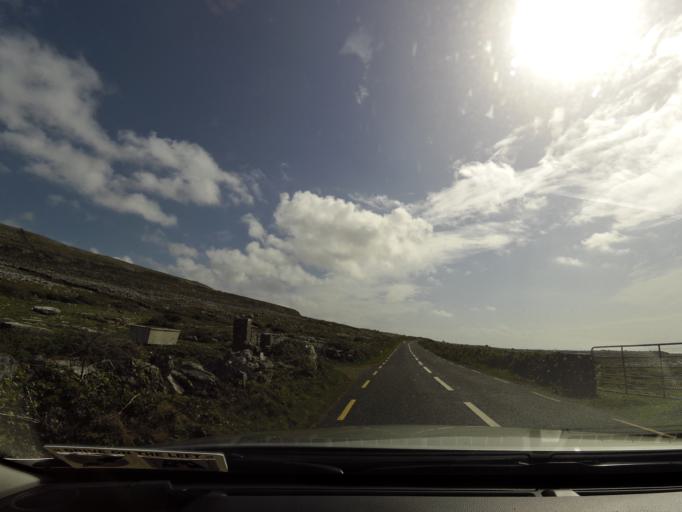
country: IE
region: Connaught
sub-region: County Galway
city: Bearna
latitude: 53.1461
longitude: -9.2720
